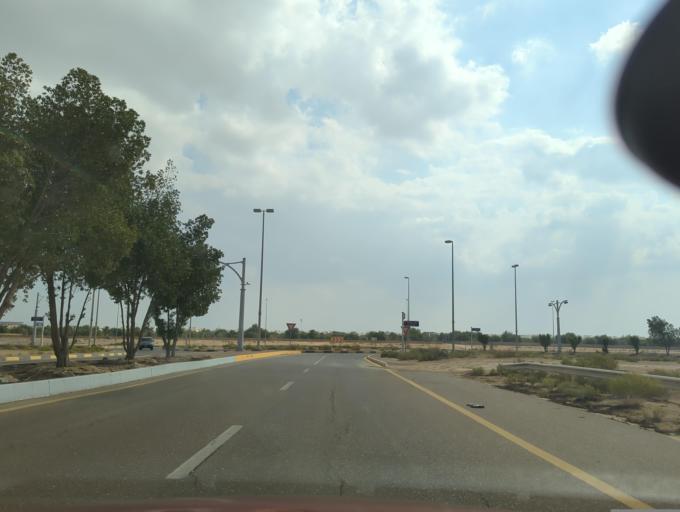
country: AE
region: Abu Dhabi
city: Abu Dhabi
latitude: 24.3685
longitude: 54.7220
